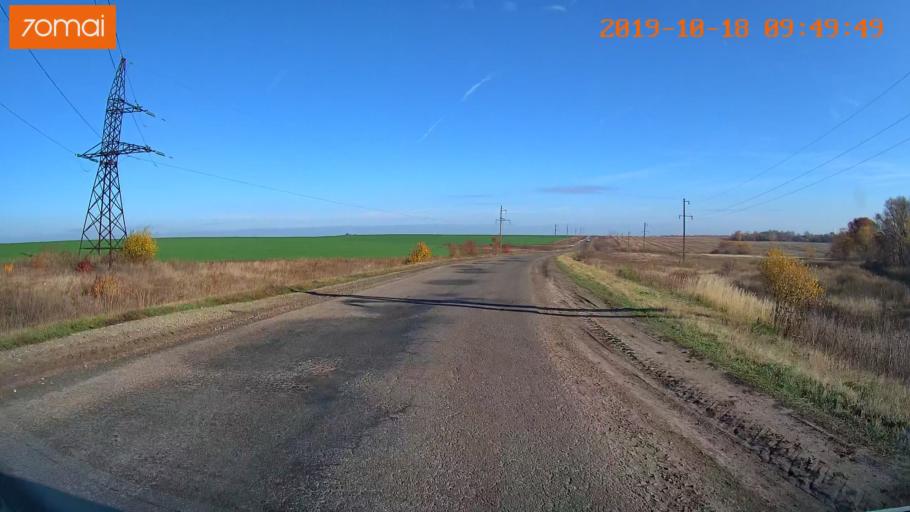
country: RU
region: Tula
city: Kazachka
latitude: 53.3221
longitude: 38.2695
